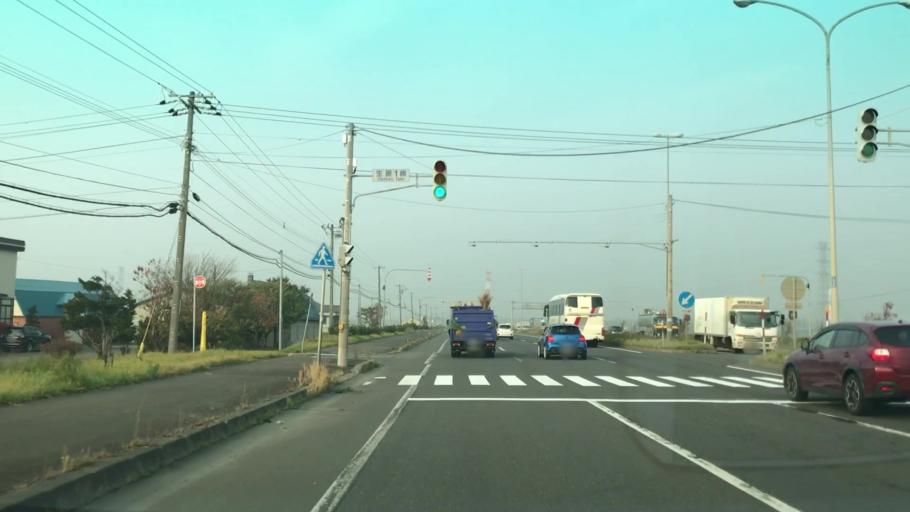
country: JP
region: Hokkaido
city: Ishikari
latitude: 43.1792
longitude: 141.3381
